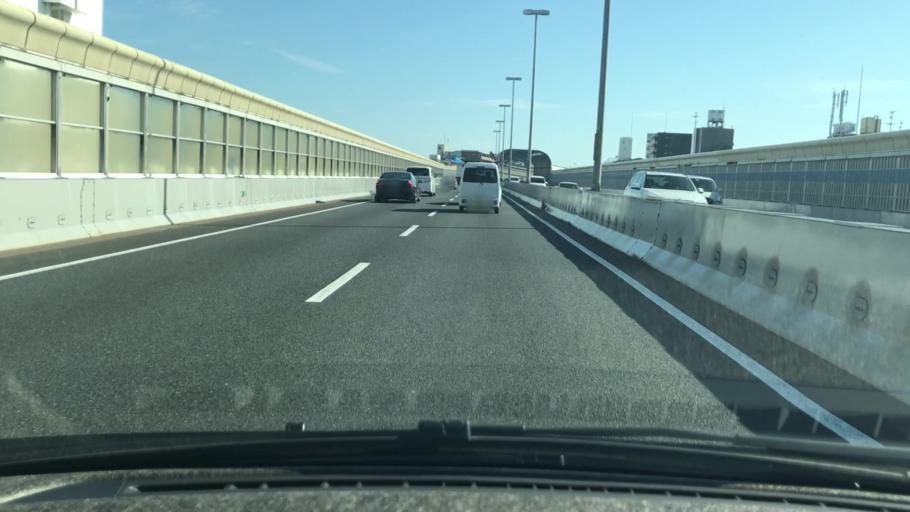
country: JP
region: Hyogo
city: Nishinomiya-hama
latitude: 34.7335
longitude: 135.3408
